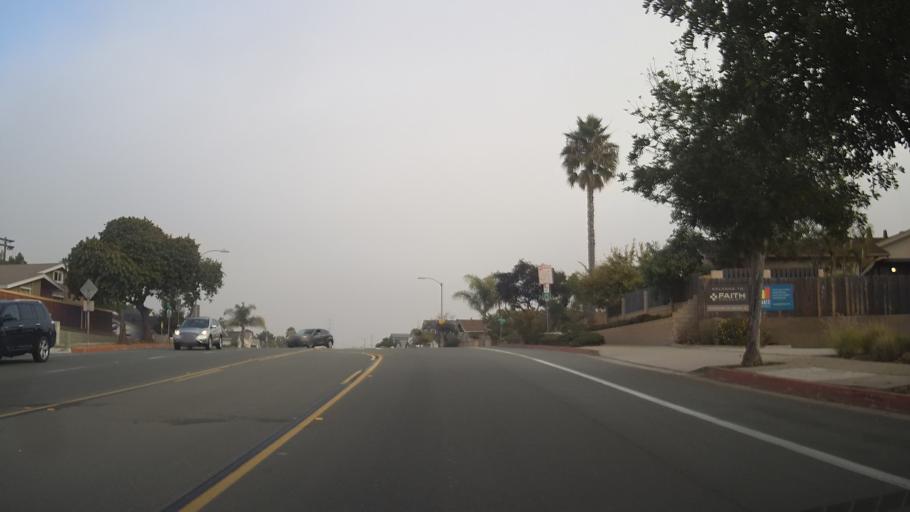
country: US
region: California
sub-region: San Diego County
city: San Diego
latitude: 32.7869
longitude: -117.1448
